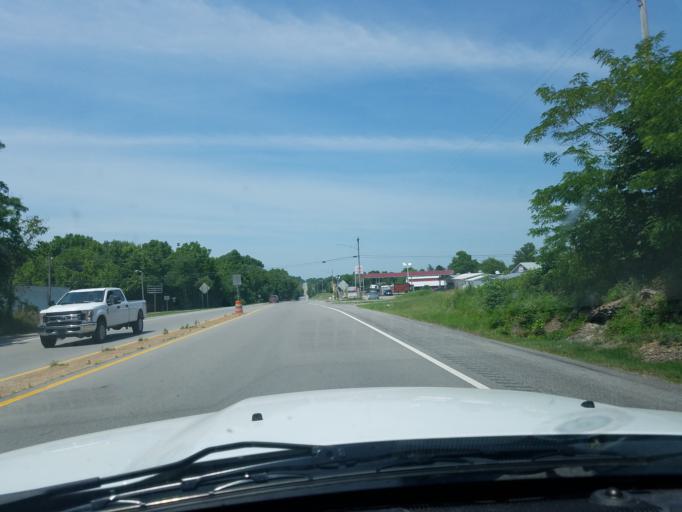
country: US
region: Tennessee
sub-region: Sumner County
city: Westmoreland
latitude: 36.5599
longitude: -86.2401
